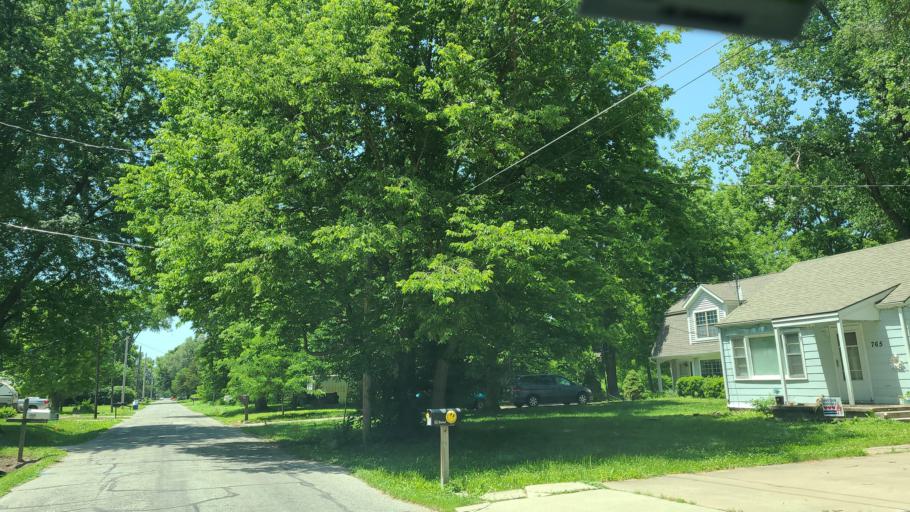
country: US
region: Kansas
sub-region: Douglas County
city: Lawrence
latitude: 38.9751
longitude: -95.2203
